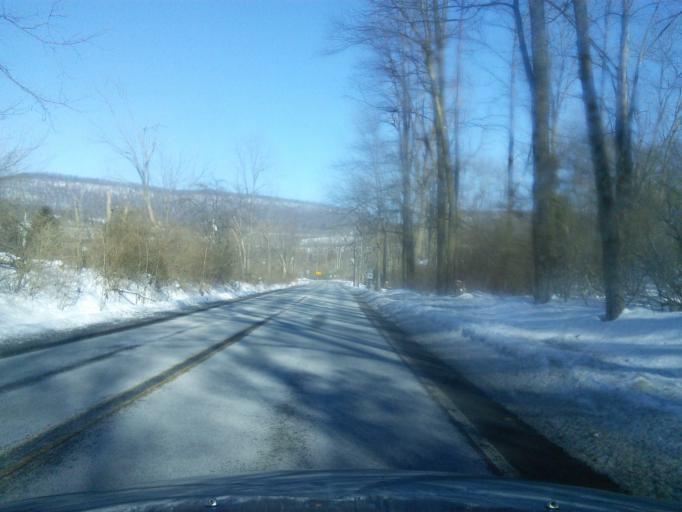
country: US
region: Pennsylvania
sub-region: Centre County
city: Park Forest Village
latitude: 40.8523
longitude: -77.8855
